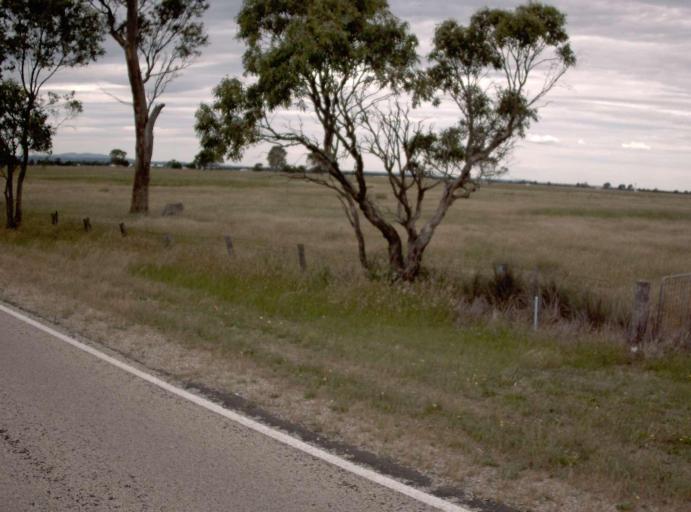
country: AU
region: Victoria
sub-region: East Gippsland
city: Bairnsdale
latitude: -37.8923
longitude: 147.5562
